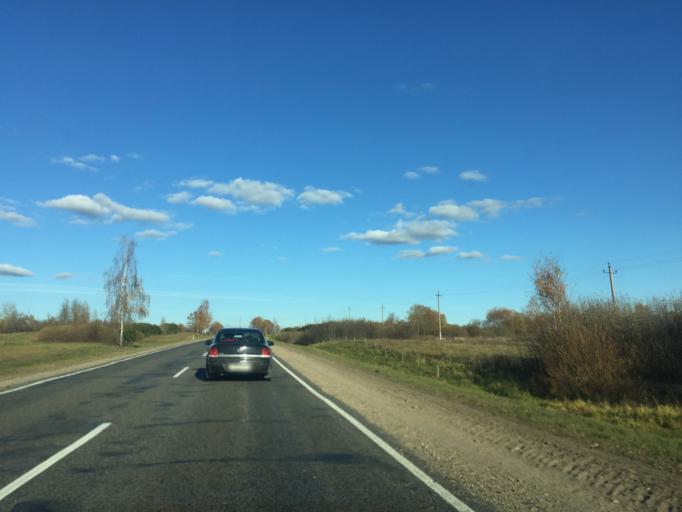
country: BY
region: Vitebsk
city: Dzisna
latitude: 55.2575
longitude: 28.1180
